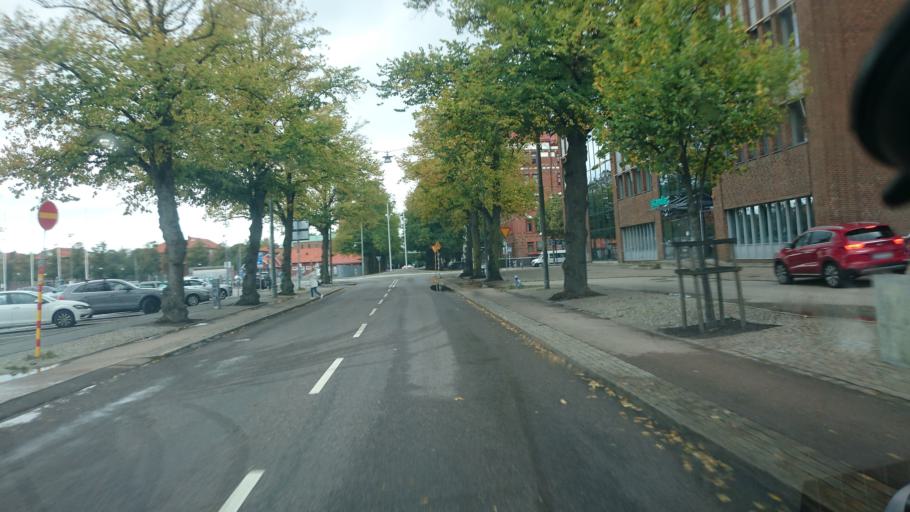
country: SE
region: Vaestra Goetaland
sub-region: Goteborg
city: Goeteborg
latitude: 57.7025
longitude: 11.9813
